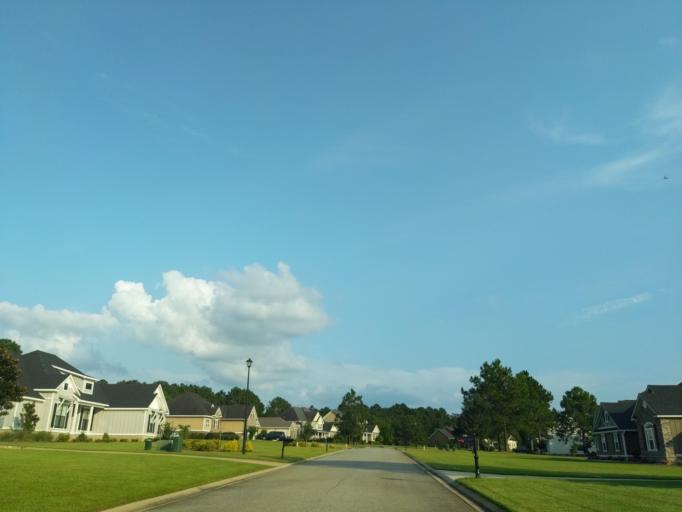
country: US
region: Georgia
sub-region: Thomas County
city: Thomasville
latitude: 30.8977
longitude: -83.9403
